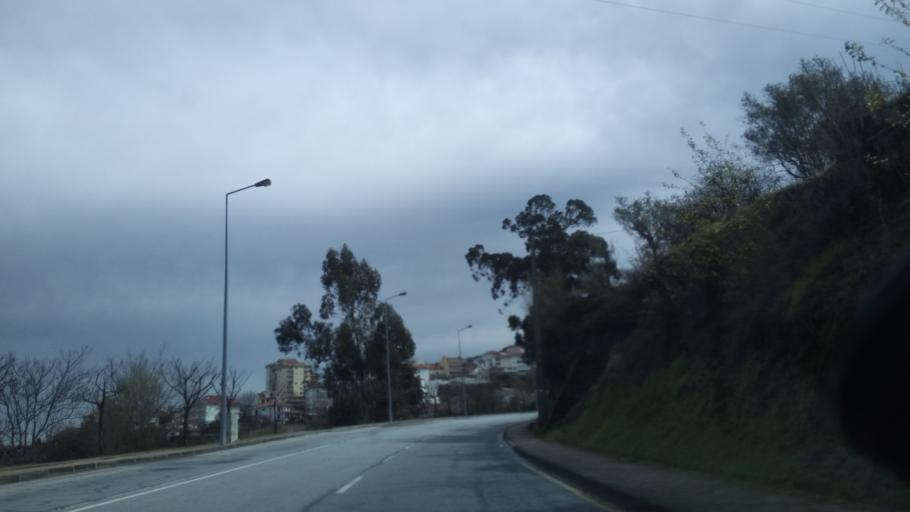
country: PT
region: Guarda
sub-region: Seia
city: Seia
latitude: 40.4207
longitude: -7.7102
